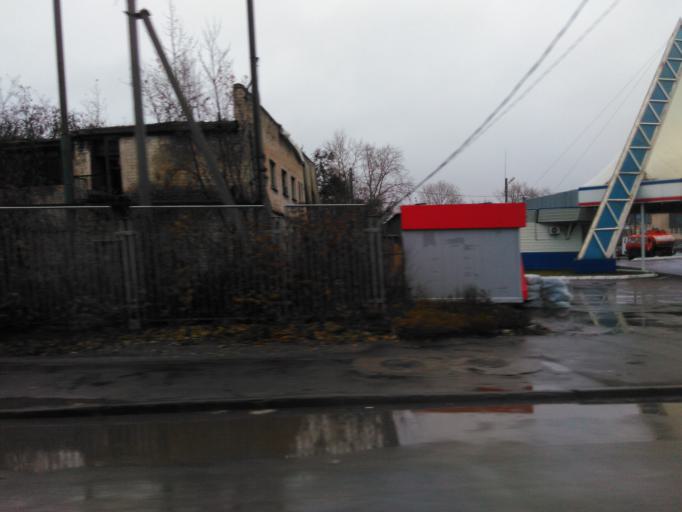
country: RU
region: Tatarstan
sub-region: Gorod Kazan'
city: Kazan
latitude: 55.7942
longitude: 49.0959
